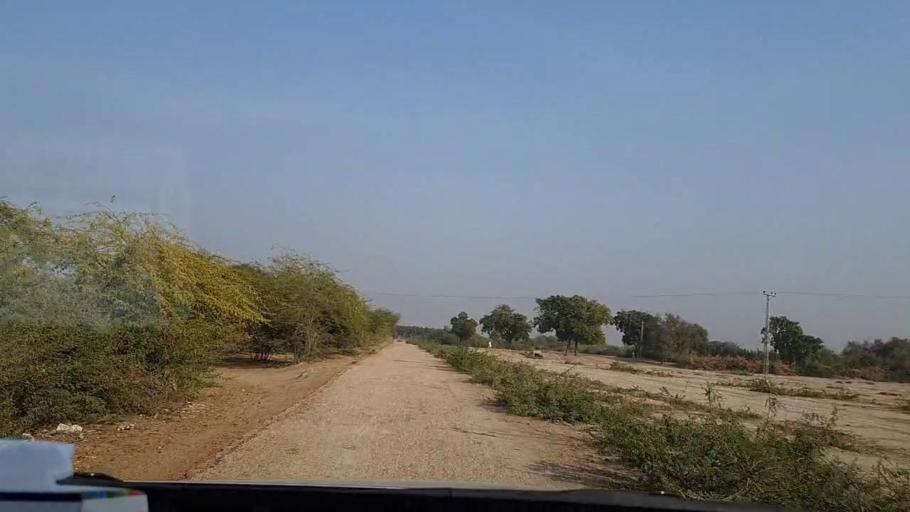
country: PK
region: Sindh
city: Tando Ghulam Ali
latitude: 25.2075
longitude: 68.8756
